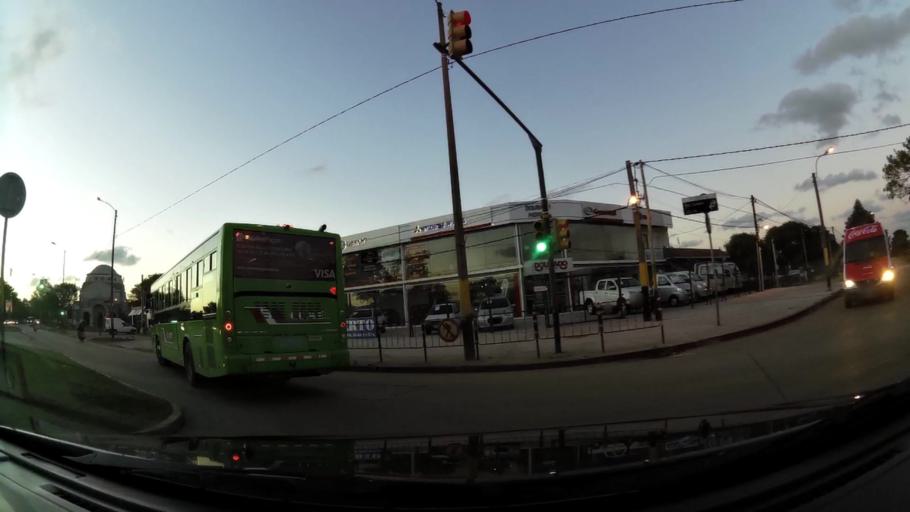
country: UY
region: Canelones
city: Paso de Carrasco
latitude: -34.8724
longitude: -56.0961
